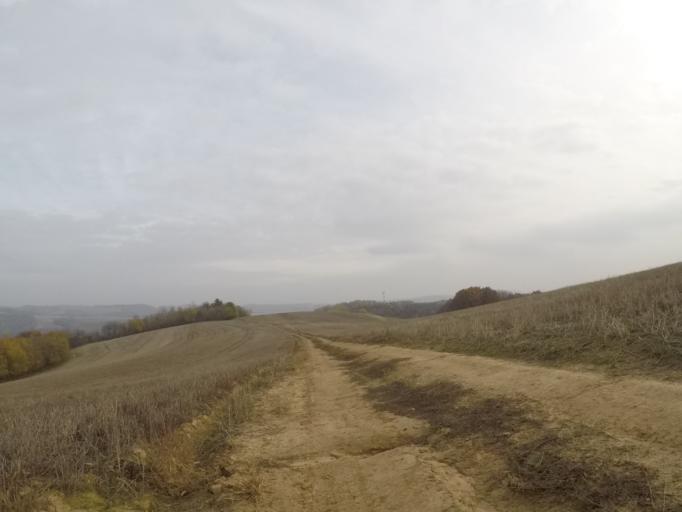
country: SK
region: Presovsky
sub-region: Okres Presov
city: Presov
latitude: 48.9388
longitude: 21.1599
